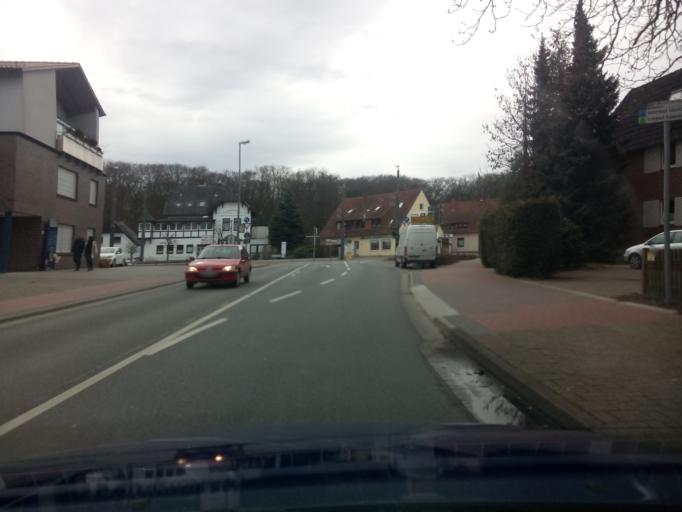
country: DE
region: Lower Saxony
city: Lilienthal
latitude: 53.1474
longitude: 8.9104
